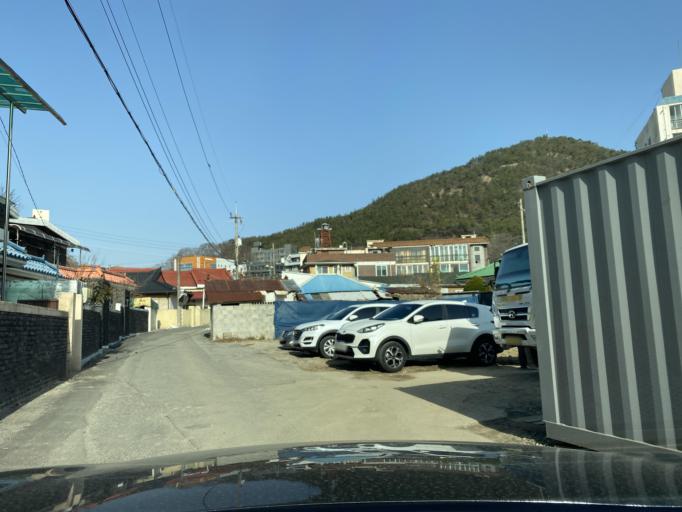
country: KR
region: Chungcheongnam-do
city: Yesan
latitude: 36.6832
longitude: 126.8463
